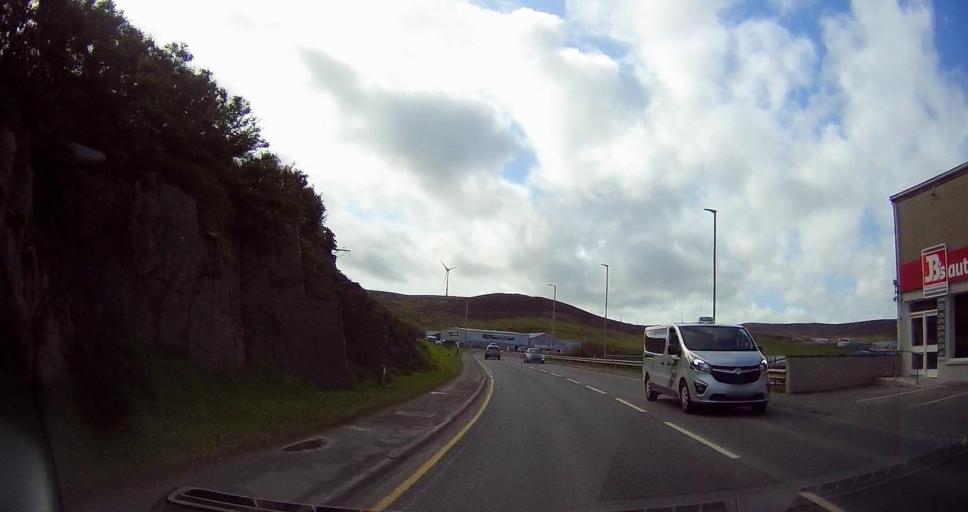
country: GB
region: Scotland
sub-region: Shetland Islands
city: Lerwick
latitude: 60.1644
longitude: -1.1613
